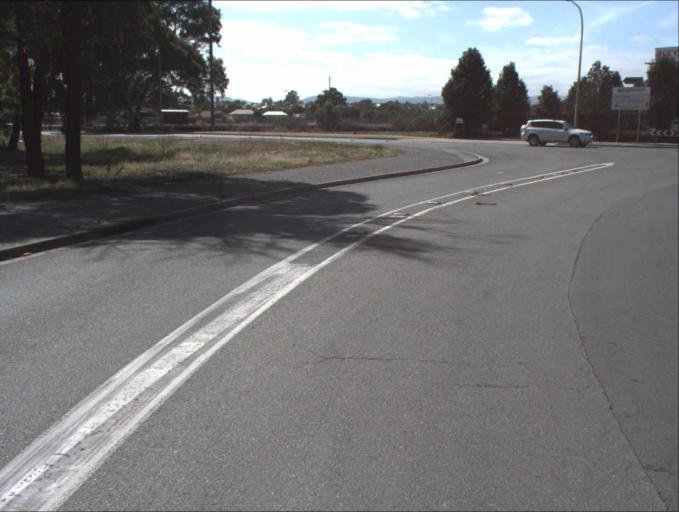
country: AU
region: South Australia
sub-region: Prospect
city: Prospect
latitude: -34.8753
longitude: 138.5804
